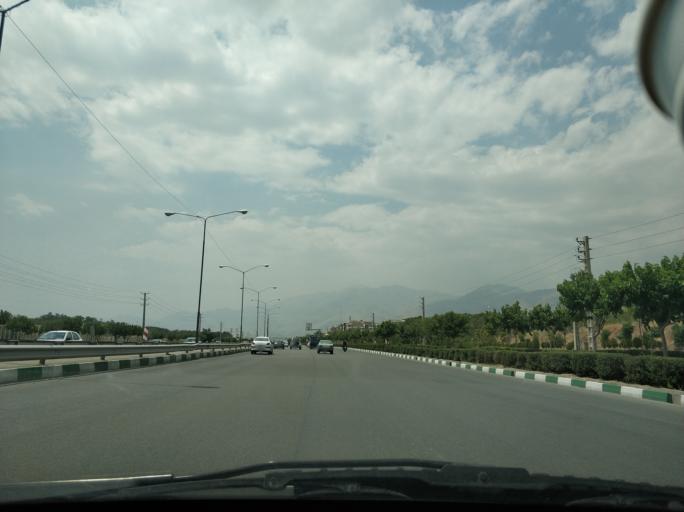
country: IR
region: Tehran
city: Tajrish
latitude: 35.7636
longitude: 51.5675
